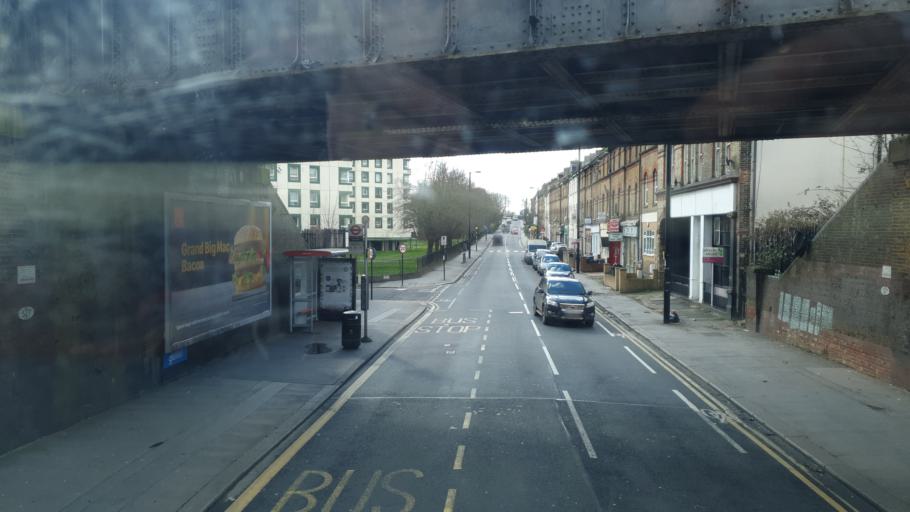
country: GB
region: England
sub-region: Greater London
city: Thornton Heath
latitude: 51.4038
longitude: -0.0686
